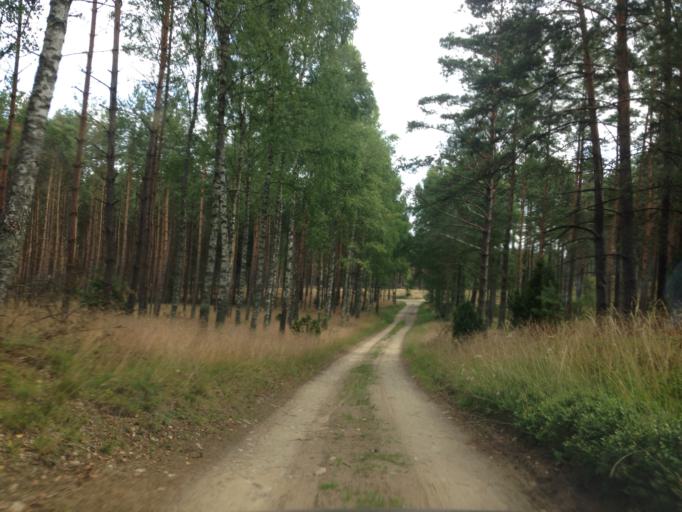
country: PL
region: Pomeranian Voivodeship
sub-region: Powiat koscierski
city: Dziemiany
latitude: 54.0609
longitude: 17.6777
